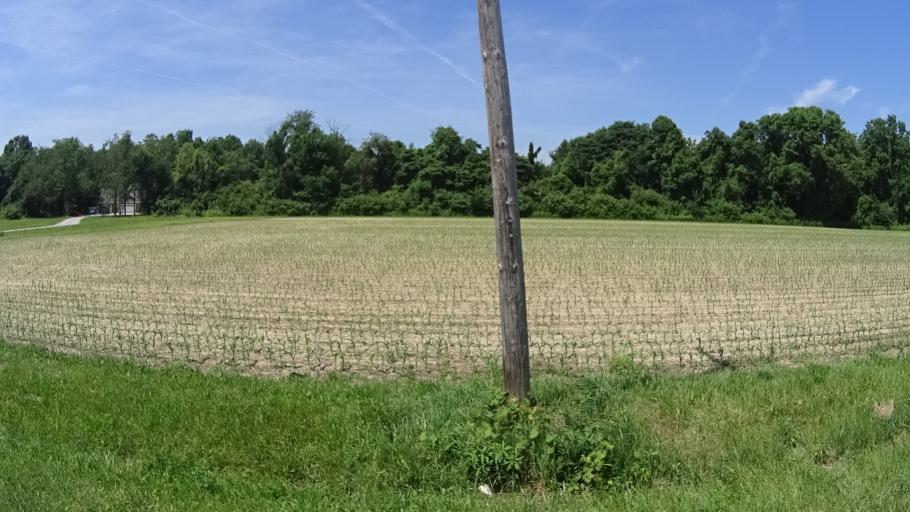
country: US
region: Ohio
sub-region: Erie County
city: Huron
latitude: 41.3424
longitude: -82.5104
